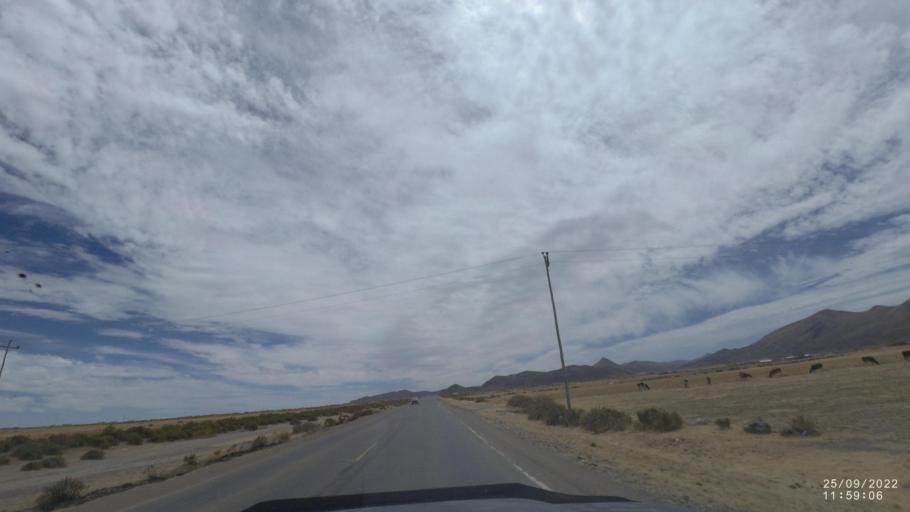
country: BO
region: Oruro
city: Challapata
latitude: -18.7931
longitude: -66.8438
